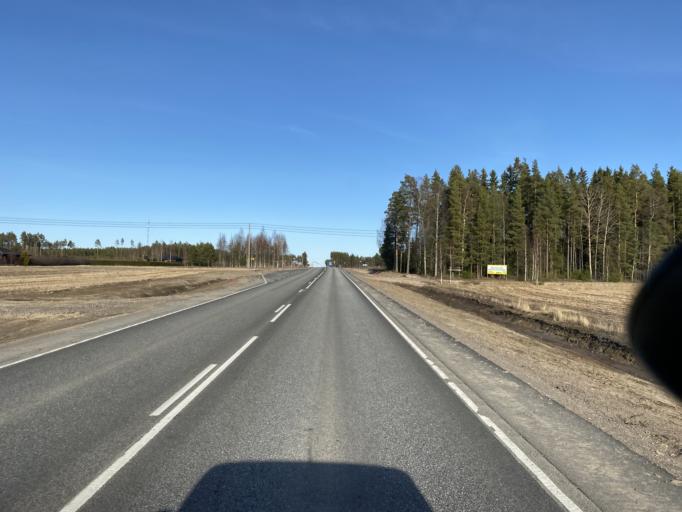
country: FI
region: Satakunta
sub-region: Rauma
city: Koeylioe
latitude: 61.1546
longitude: 22.2692
